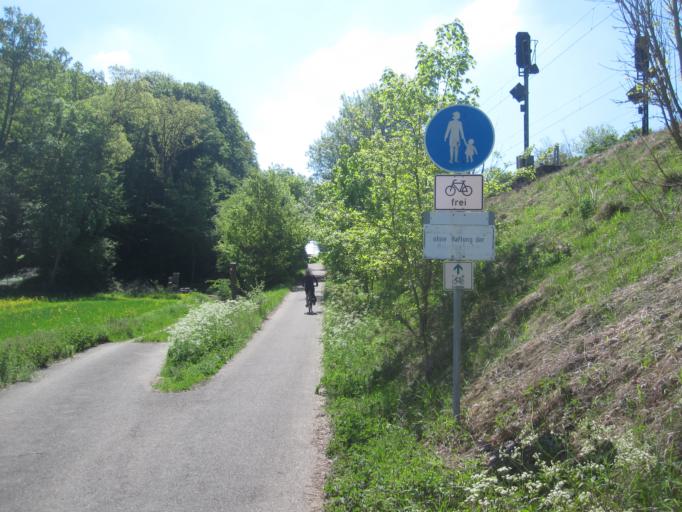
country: DE
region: Baden-Wuerttemberg
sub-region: Tuebingen Region
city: Westerstetten
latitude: 48.5273
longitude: 9.9390
